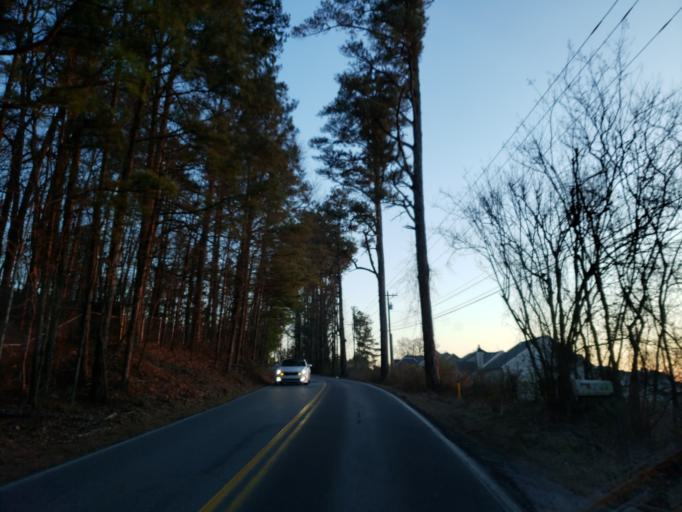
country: US
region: Georgia
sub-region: Cherokee County
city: Woodstock
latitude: 34.1007
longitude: -84.4913
